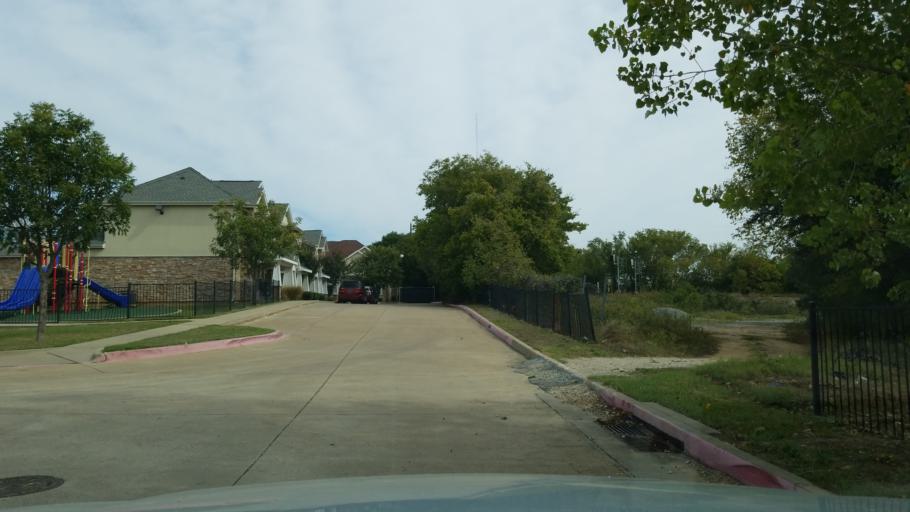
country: US
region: Texas
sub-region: Dallas County
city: Dallas
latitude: 32.7754
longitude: -96.7356
